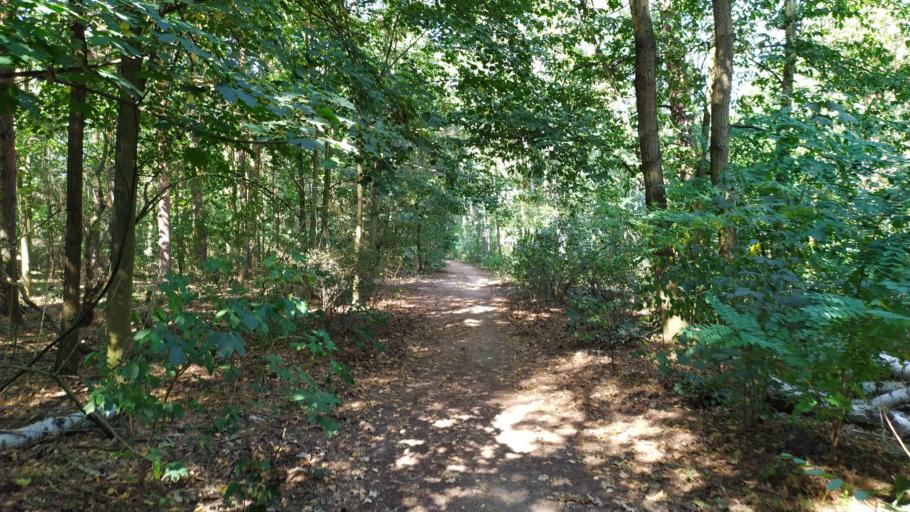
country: DE
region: Berlin
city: Berlin Koepenick
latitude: 52.4376
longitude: 13.5944
